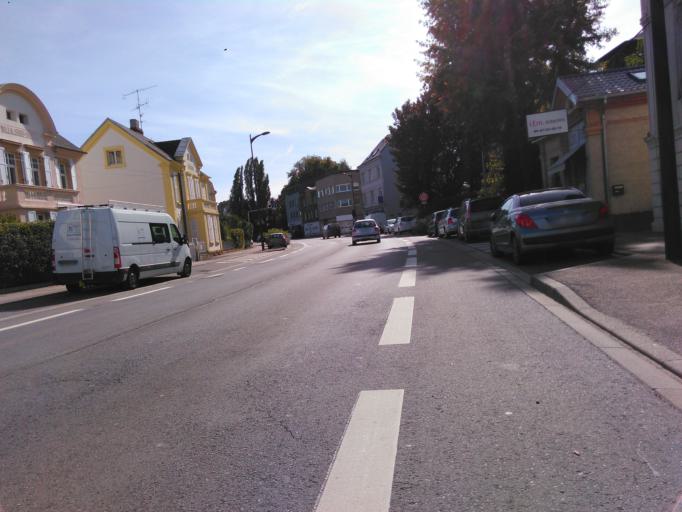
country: FR
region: Lorraine
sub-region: Departement de la Moselle
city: Thionville
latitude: 49.3660
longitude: 6.1686
